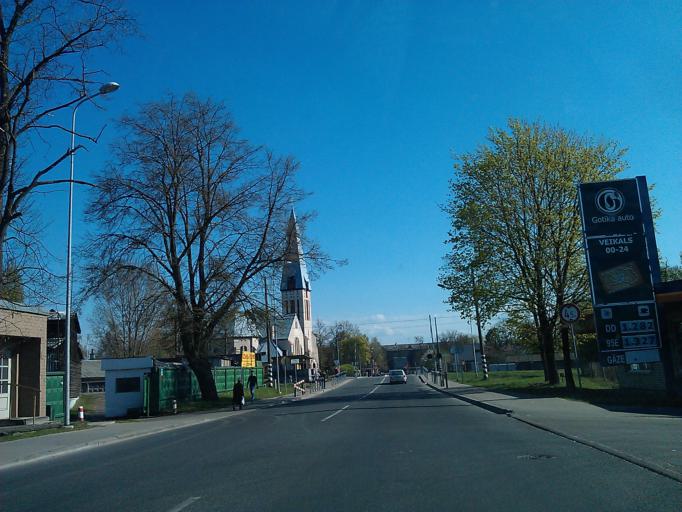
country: LV
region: Riga
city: Jaunciems
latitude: 56.9853
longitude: 24.1925
